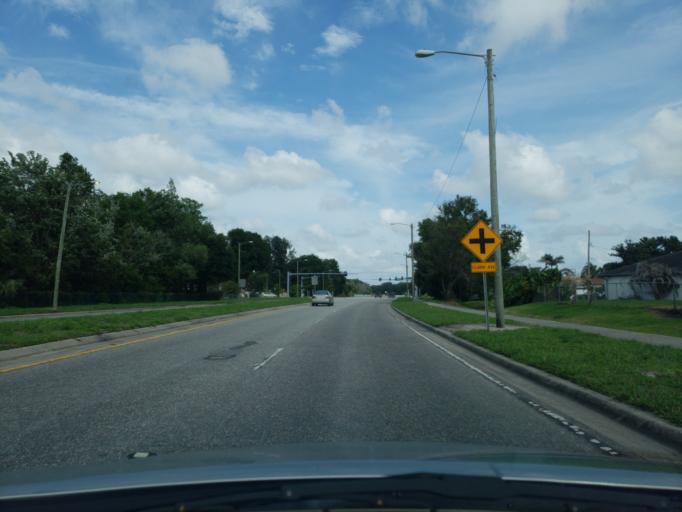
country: US
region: Florida
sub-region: Hillsborough County
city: Egypt Lake-Leto
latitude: 28.0101
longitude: -82.5133
